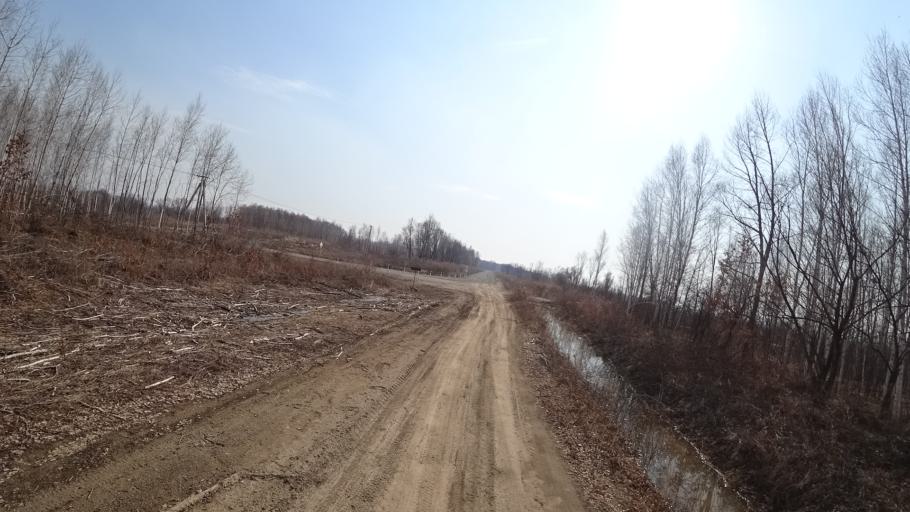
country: RU
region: Amur
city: Novobureyskiy
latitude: 49.8283
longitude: 129.9891
